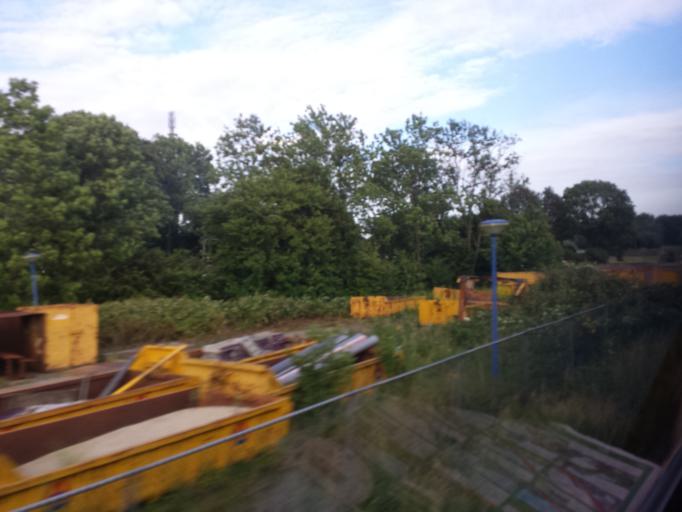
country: NL
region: South Holland
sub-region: Bodegraven-Reeuwijk
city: Bodegraven
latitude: 52.1032
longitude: 4.7191
